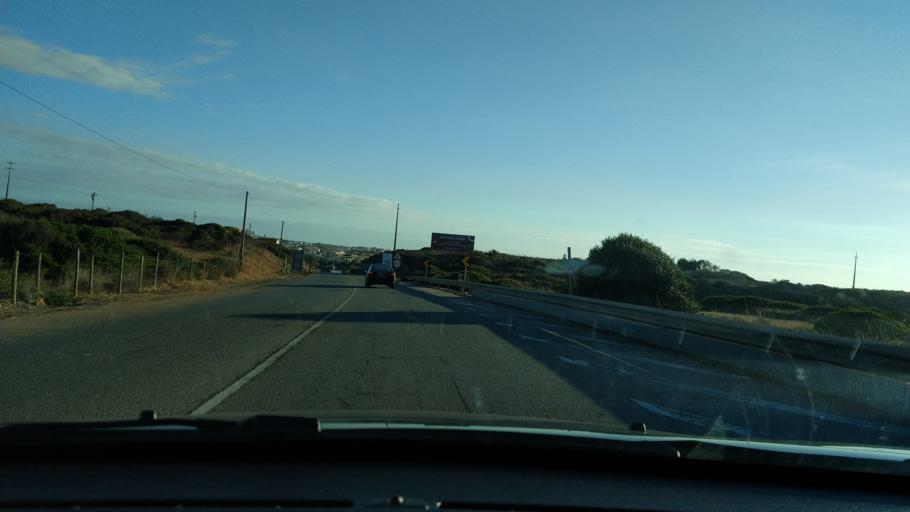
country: PT
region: Faro
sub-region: Vila do Bispo
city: Sagres
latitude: 37.0251
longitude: -8.9378
